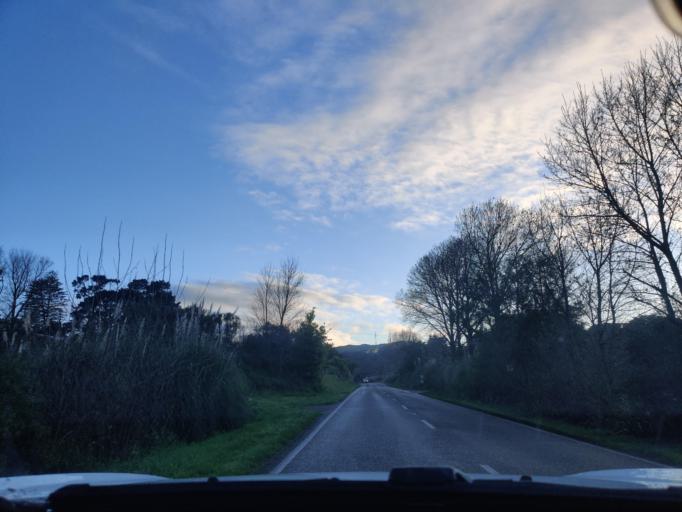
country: NZ
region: Manawatu-Wanganui
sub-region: Palmerston North City
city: Palmerston North
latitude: -40.3145
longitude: 175.7568
